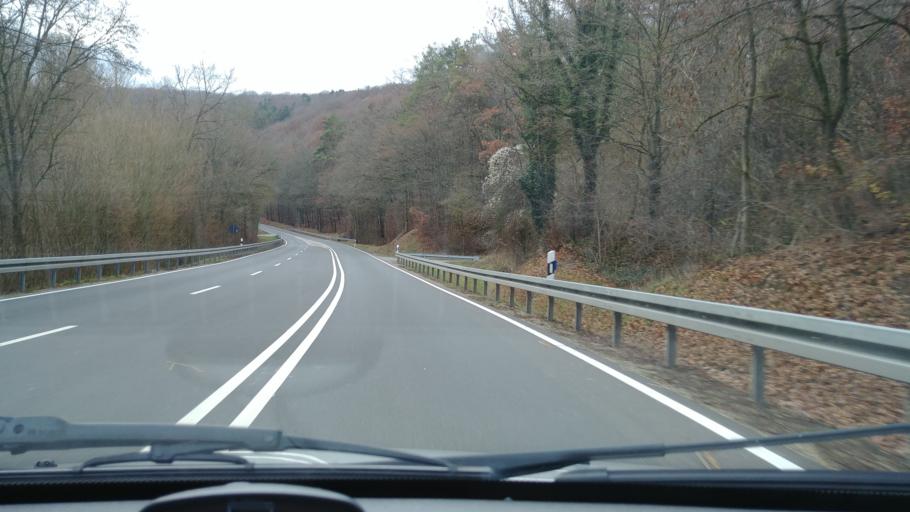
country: DE
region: Bavaria
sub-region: Regierungsbezirk Unterfranken
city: Eussenheim
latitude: 49.9550
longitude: 9.8203
